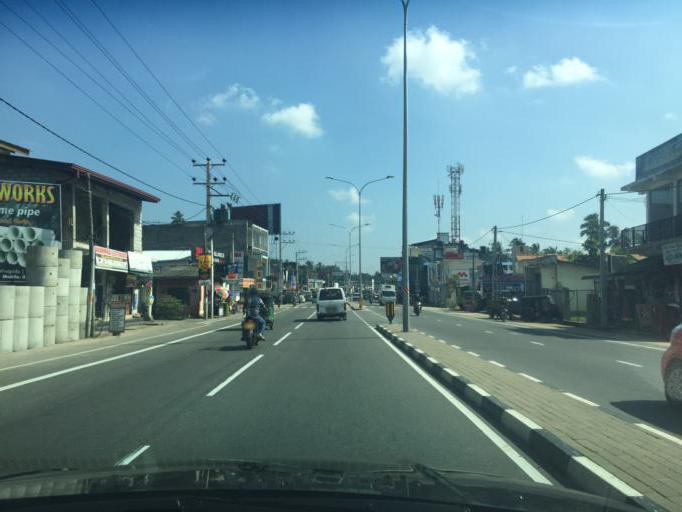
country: LK
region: Western
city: Maharagama
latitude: 6.8212
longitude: 79.9161
